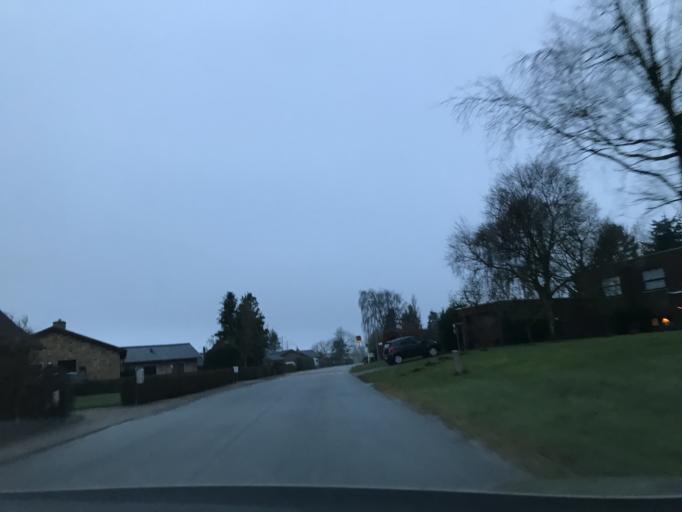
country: DK
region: Central Jutland
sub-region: Hedensted Kommune
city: Hornsyld
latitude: 55.7001
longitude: 9.7876
